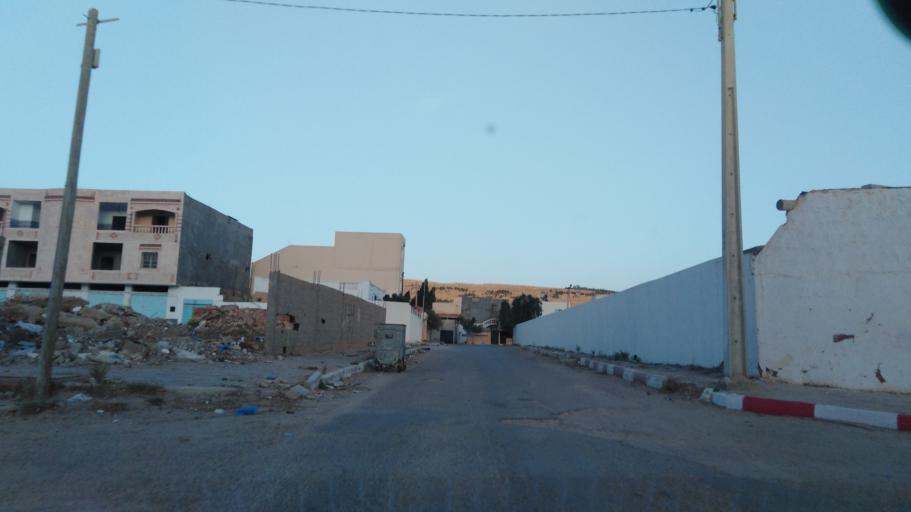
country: TN
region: Tataouine
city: Tataouine
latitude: 32.9403
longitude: 10.4543
